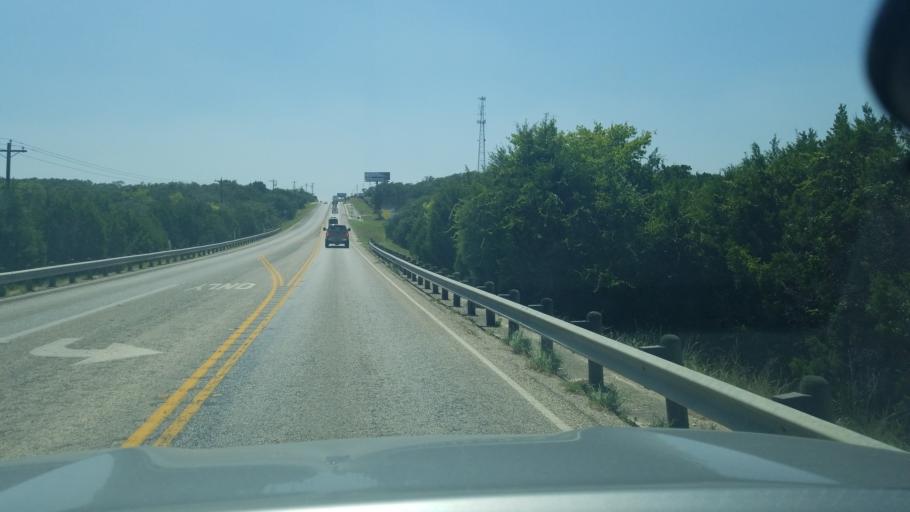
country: US
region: Texas
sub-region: Bexar County
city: Fair Oaks Ranch
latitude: 29.8145
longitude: -98.6233
